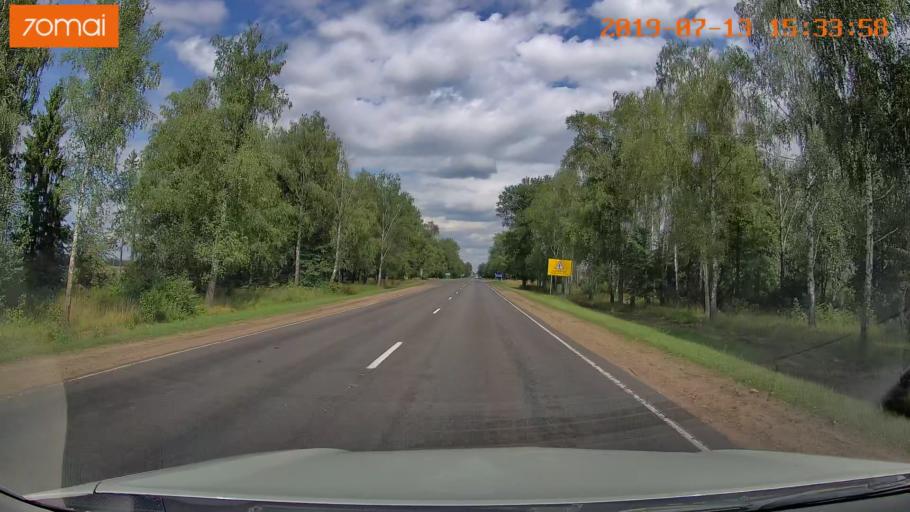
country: BY
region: Mogilev
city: Babruysk
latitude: 53.1202
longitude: 29.1483
